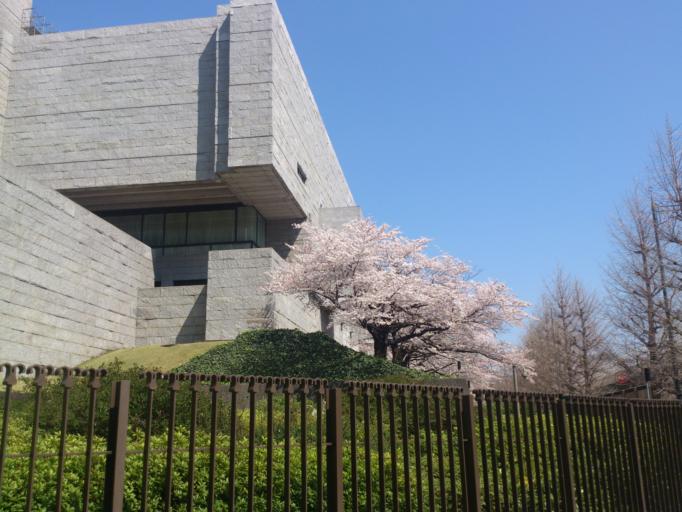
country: JP
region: Tokyo
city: Tokyo
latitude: 35.6796
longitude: 139.7430
